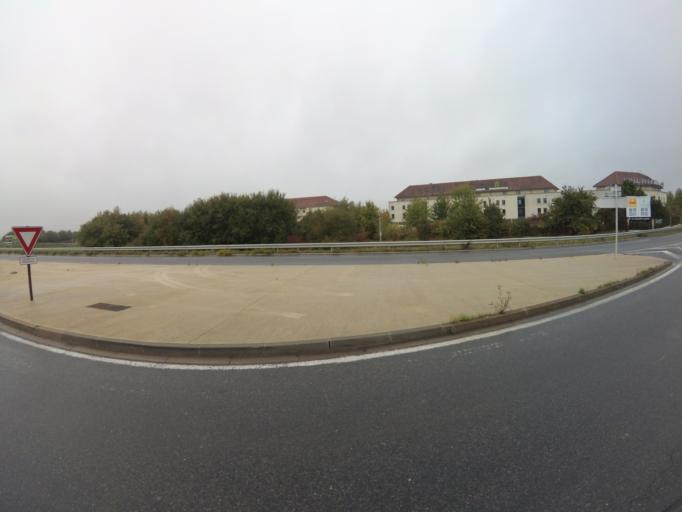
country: FR
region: Ile-de-France
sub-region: Departement de Seine-et-Marne
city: Ferrieres-en-Brie
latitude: 48.8314
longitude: 2.7060
